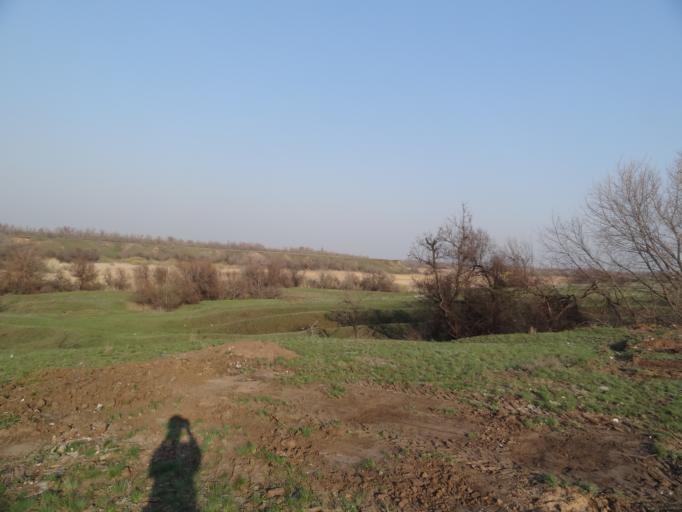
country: RU
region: Saratov
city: Privolzhskiy
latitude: 51.3319
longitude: 46.0368
